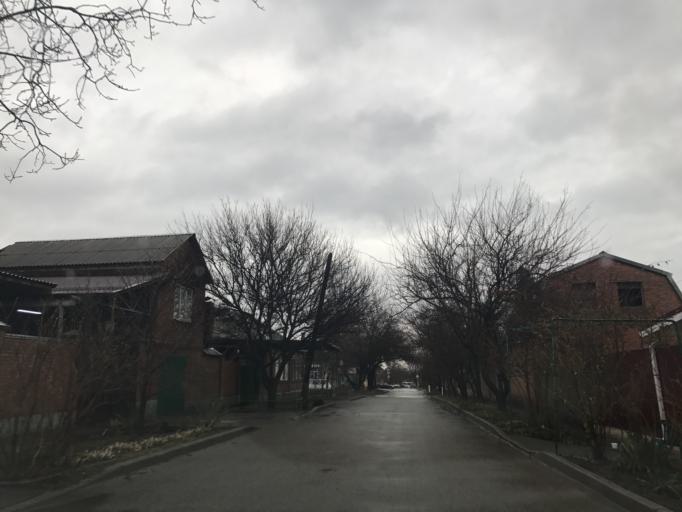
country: RU
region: Rostov
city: Rostov-na-Donu
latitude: 47.2238
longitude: 39.6503
